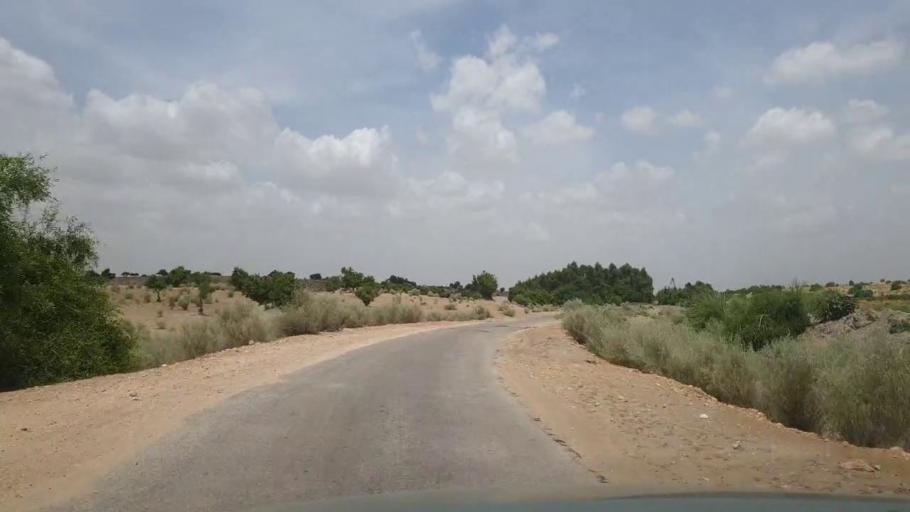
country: PK
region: Sindh
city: Kot Diji
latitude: 27.2028
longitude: 69.0837
